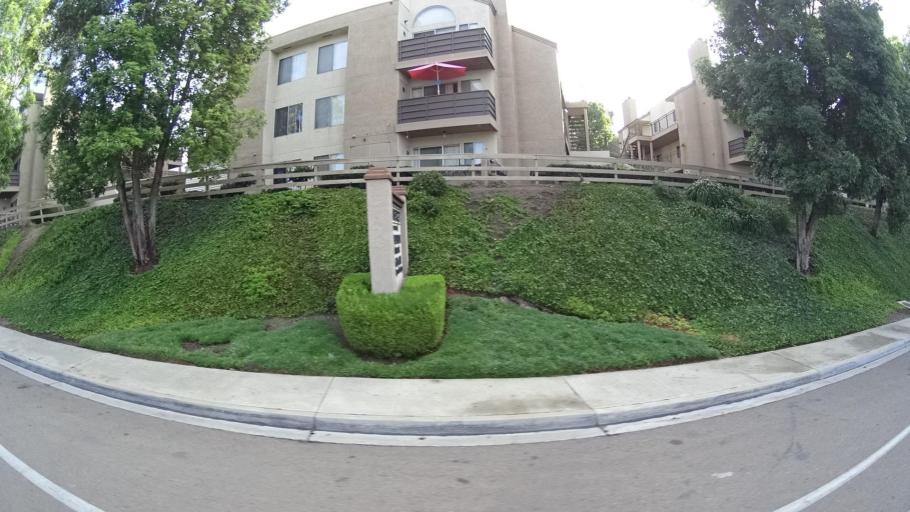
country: US
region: California
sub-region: San Diego County
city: Casa de Oro-Mount Helix
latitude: 32.7381
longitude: -116.9721
